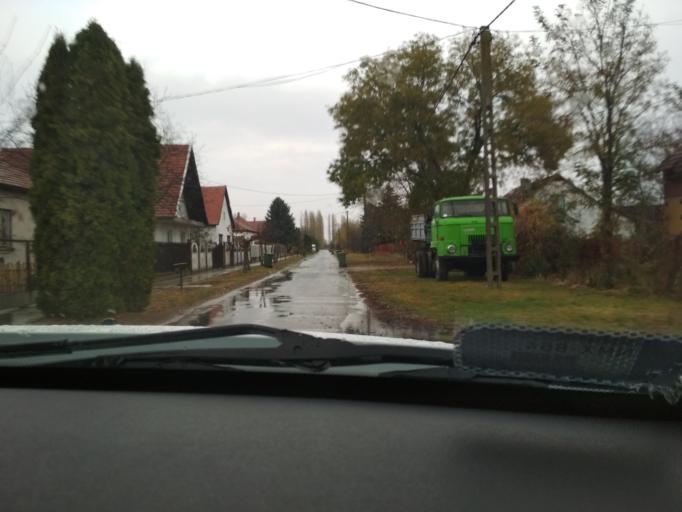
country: HU
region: Csongrad
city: Opusztaszer
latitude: 46.4334
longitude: 20.1362
